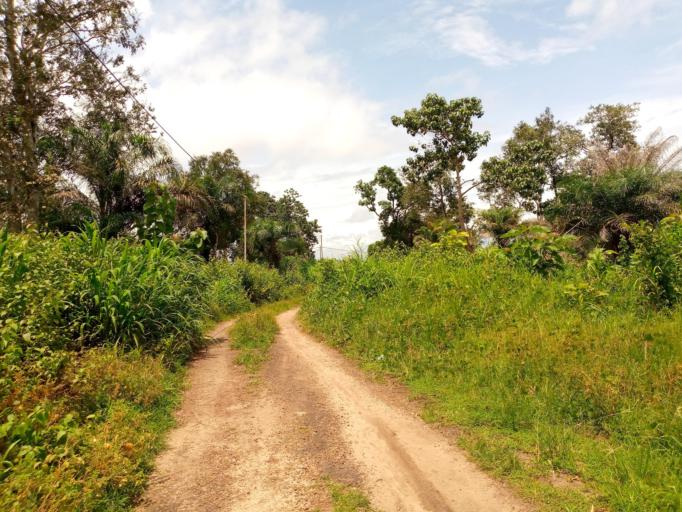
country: SL
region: Northern Province
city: Magburaka
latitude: 8.7264
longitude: -11.9267
